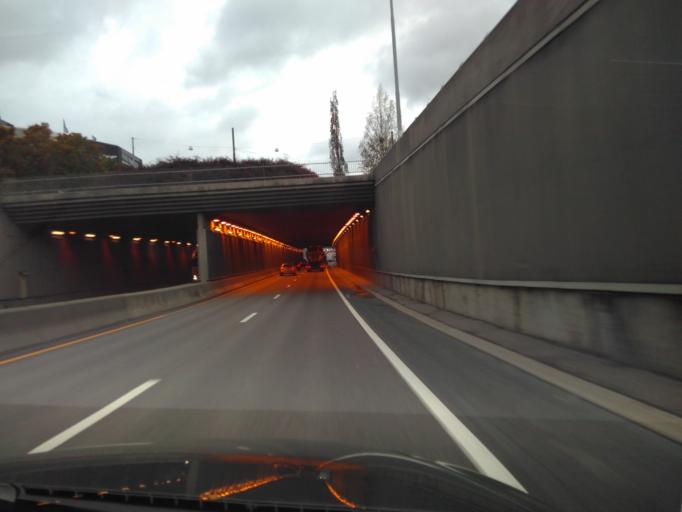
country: NO
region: Oslo
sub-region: Oslo
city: Oslo
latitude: 59.9446
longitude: 10.7797
